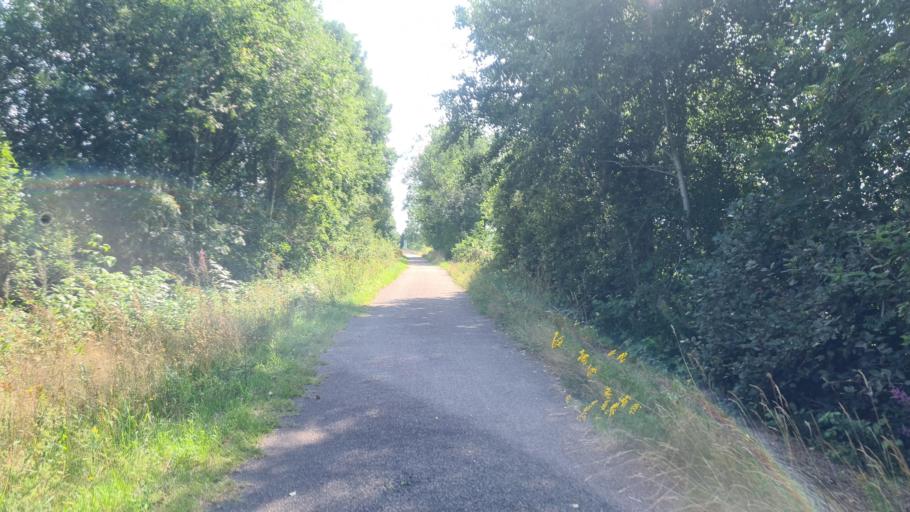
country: SE
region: Kronoberg
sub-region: Ljungby Kommun
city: Ljungby
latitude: 56.7955
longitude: 13.9091
